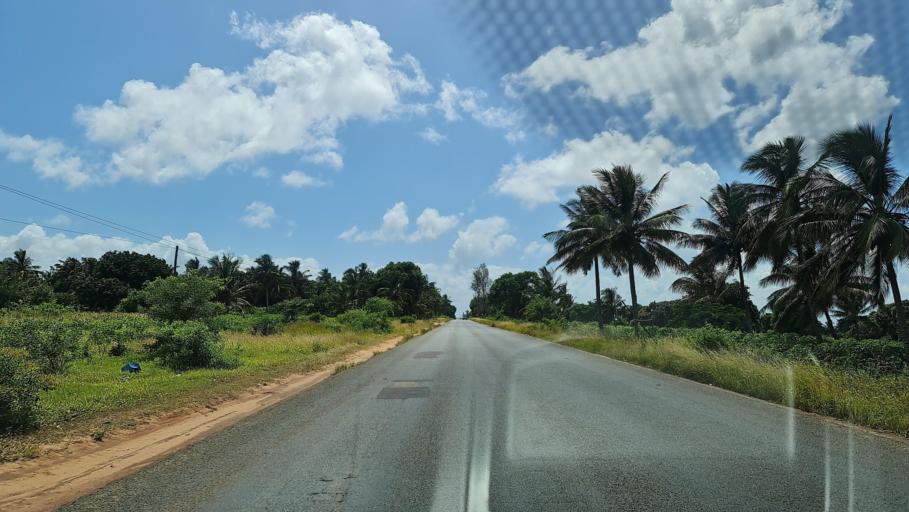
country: MZ
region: Inhambane
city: Maxixe
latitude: -24.5280
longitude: 34.9541
